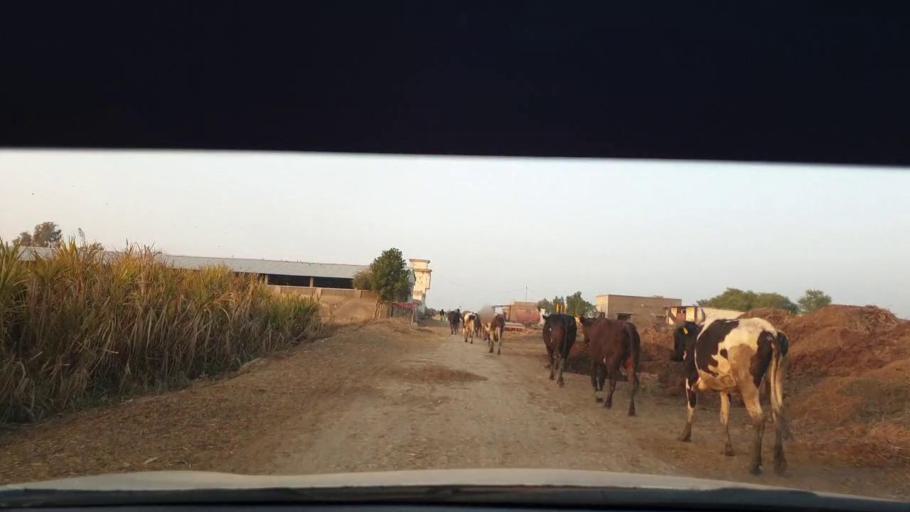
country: PK
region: Sindh
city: Berani
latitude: 25.7542
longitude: 69.0073
